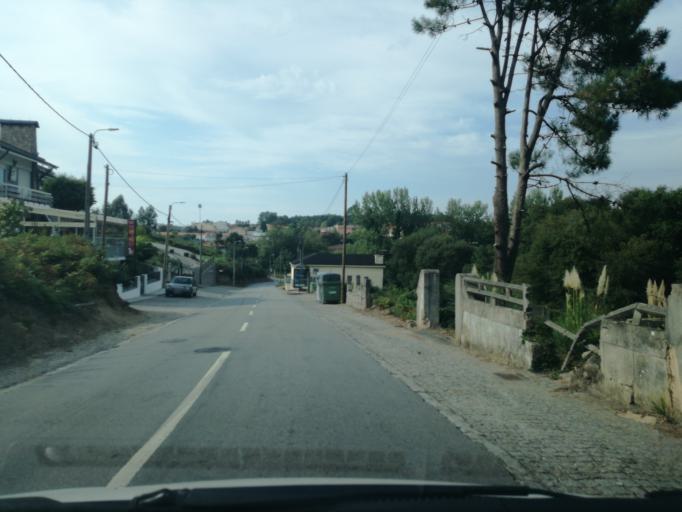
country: PT
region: Porto
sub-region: Vila Nova de Gaia
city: Sao Felix da Marinha
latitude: 41.0307
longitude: -8.6300
